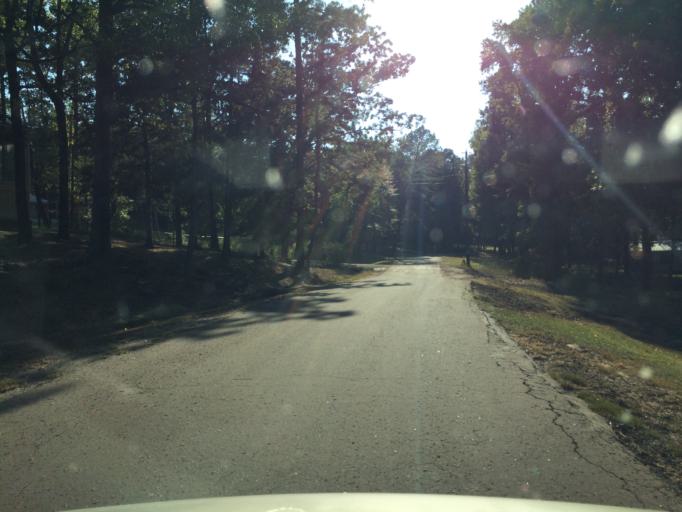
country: US
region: Texas
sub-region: Wood County
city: Hawkins
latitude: 32.6190
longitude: -95.2563
